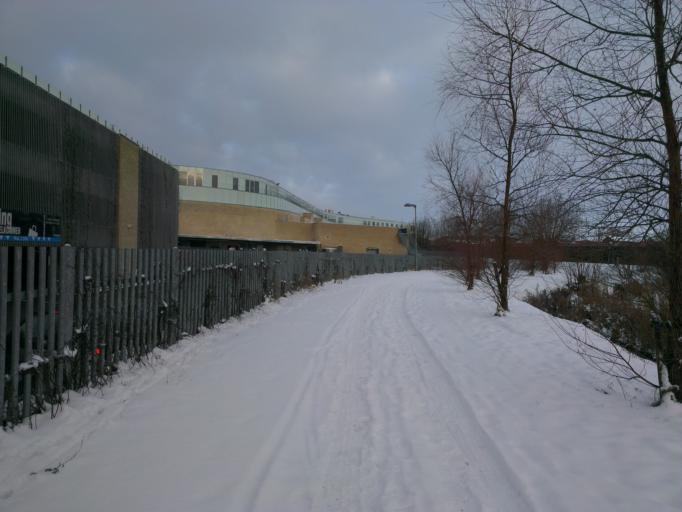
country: DK
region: Capital Region
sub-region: Frederikssund Kommune
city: Frederikssund
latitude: 55.8345
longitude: 12.0652
